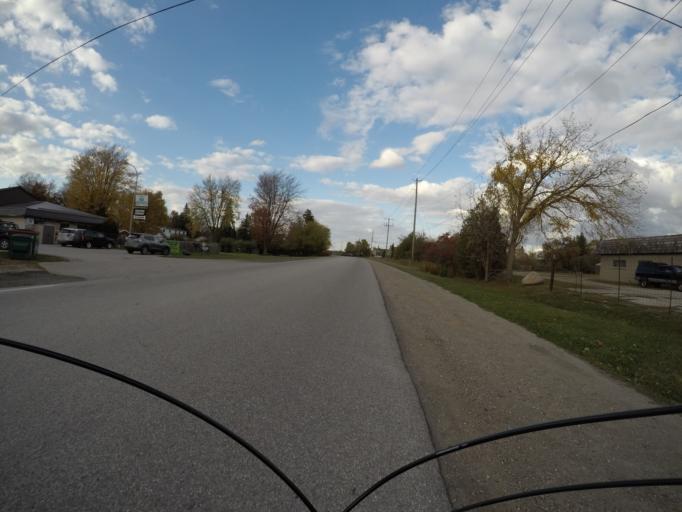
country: CA
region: Ontario
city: Waterloo
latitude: 43.5456
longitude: -80.5524
